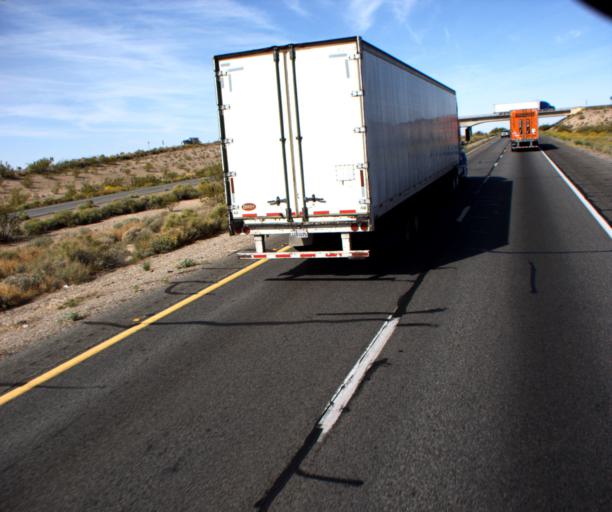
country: US
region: Arizona
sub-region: Maricopa County
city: Buckeye
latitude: 33.4623
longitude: -112.7790
